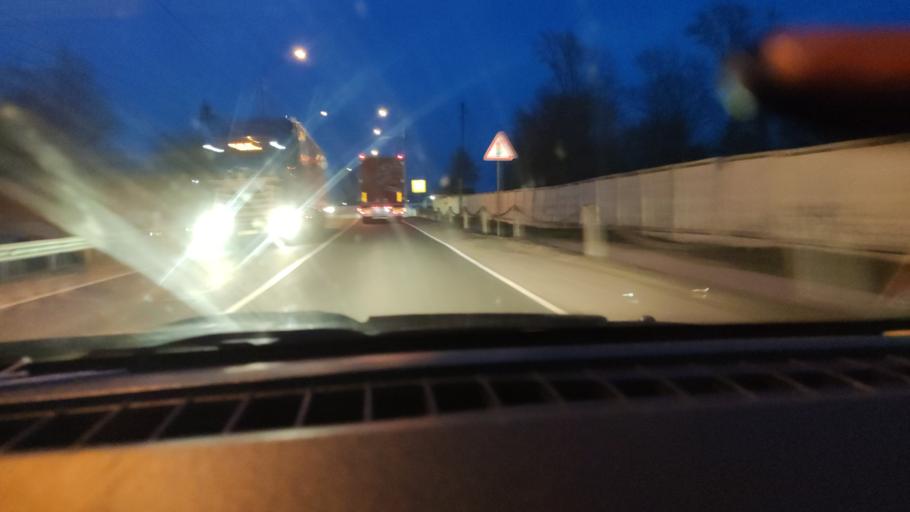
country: RU
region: Saratov
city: Sennoy
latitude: 52.1521
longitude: 46.9641
